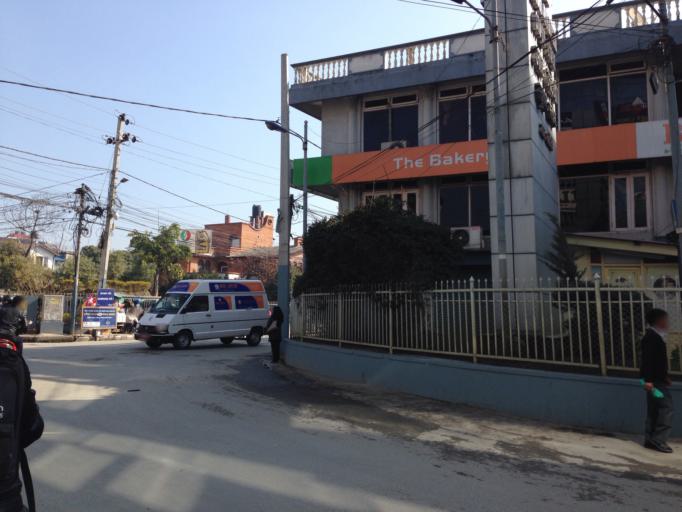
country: NP
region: Central Region
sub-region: Bagmati Zone
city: Kathmandu
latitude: 27.7190
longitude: 85.3311
